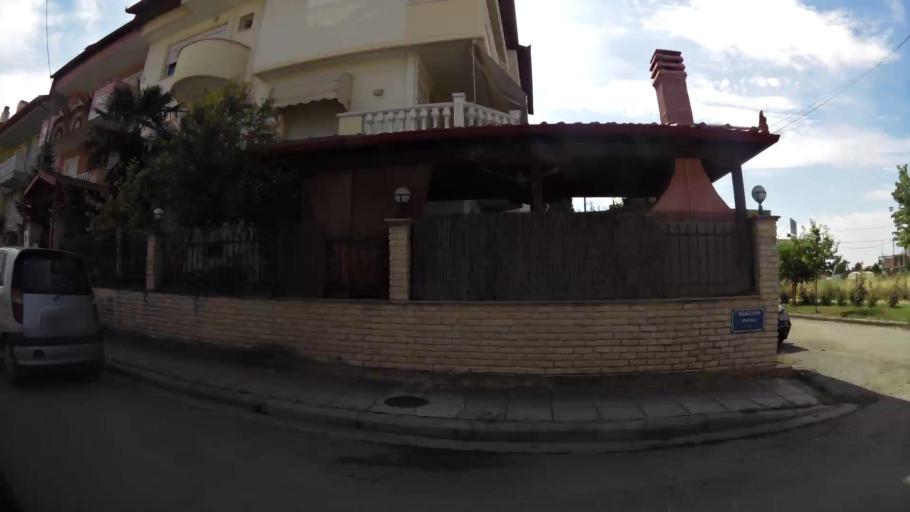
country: GR
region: Central Macedonia
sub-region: Nomos Pierias
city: Katerini
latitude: 40.2842
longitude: 22.5091
